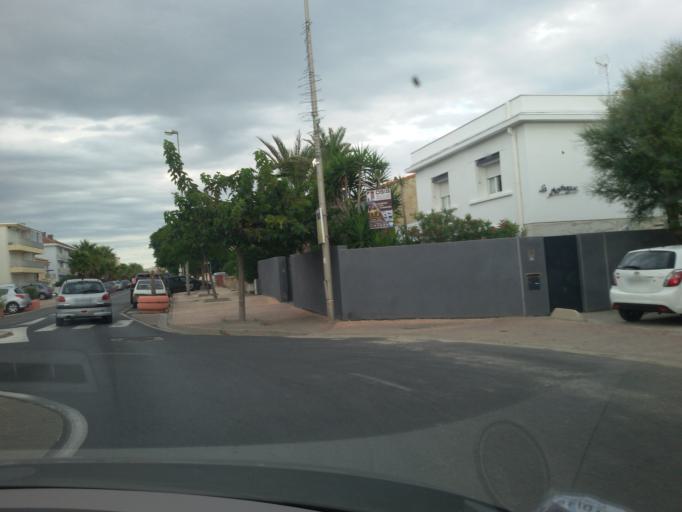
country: FR
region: Languedoc-Roussillon
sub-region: Departement de l'Herault
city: Perols
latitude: 43.5398
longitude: 3.9649
